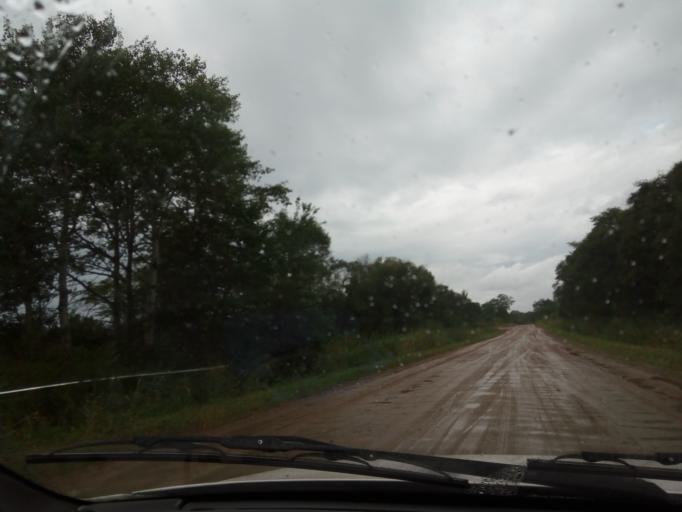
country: RU
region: Primorskiy
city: Lazo
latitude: 45.8546
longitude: 133.6467
